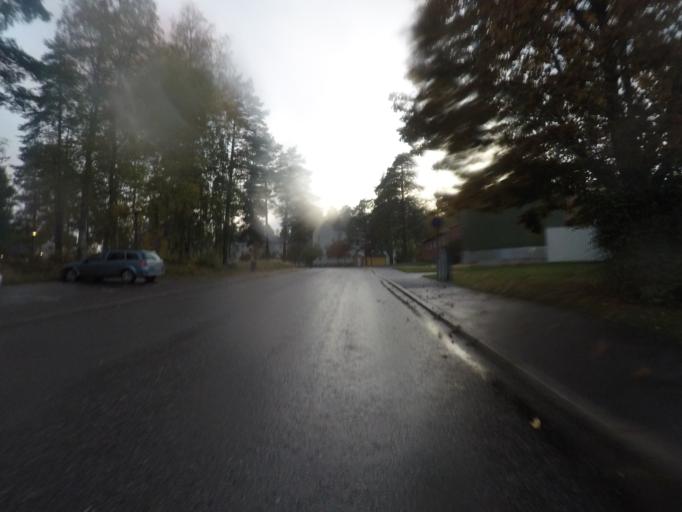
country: SE
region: OErebro
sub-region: Karlskoga Kommun
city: Karlskoga
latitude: 59.3187
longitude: 14.4910
